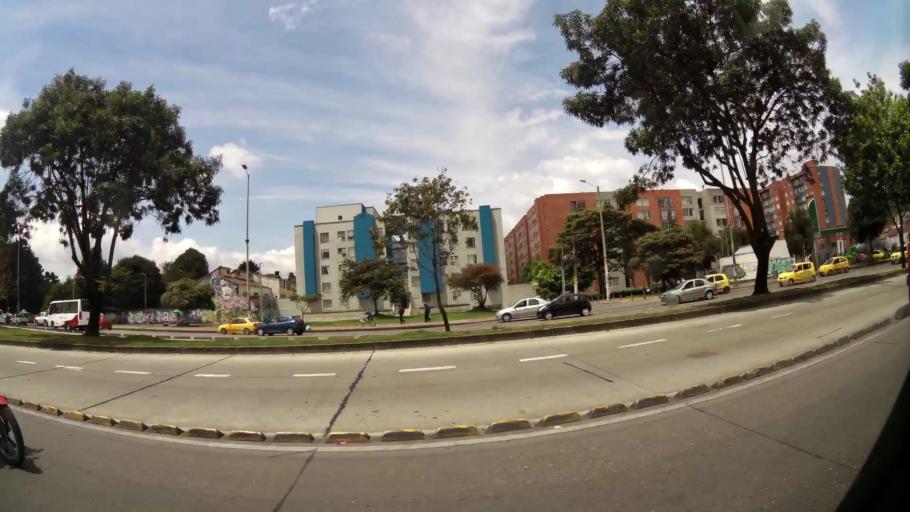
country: CO
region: Cundinamarca
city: Cota
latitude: 4.7412
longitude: -74.0895
